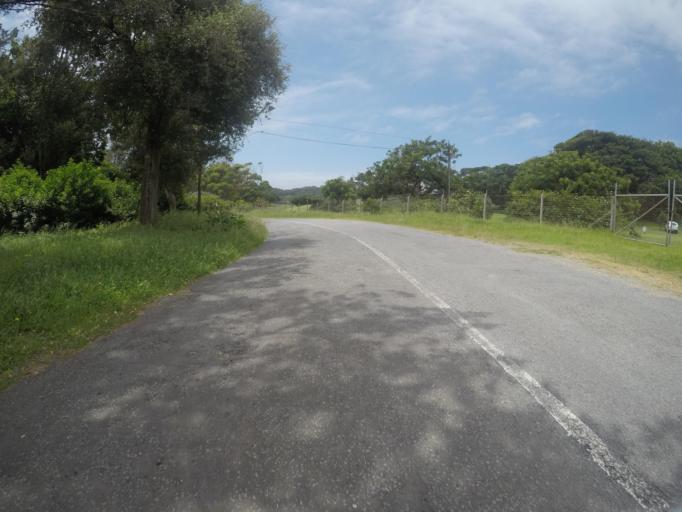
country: ZA
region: Eastern Cape
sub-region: Buffalo City Metropolitan Municipality
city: East London
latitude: -32.9947
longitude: 27.9359
